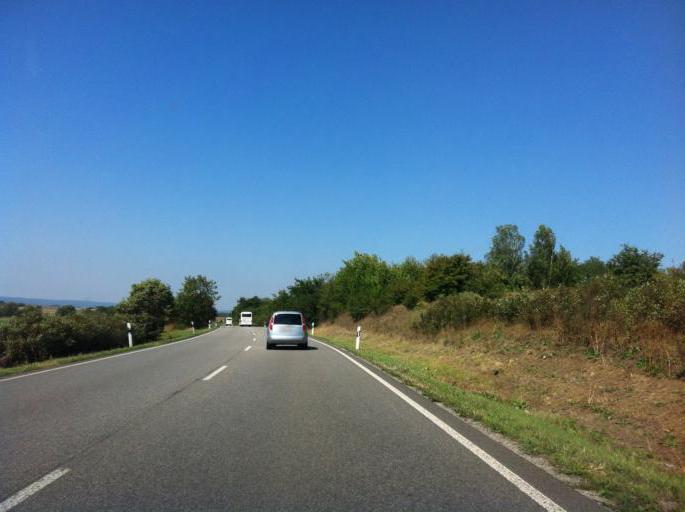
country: DE
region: Thuringia
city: Grossengottern
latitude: 51.1250
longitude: 10.6001
